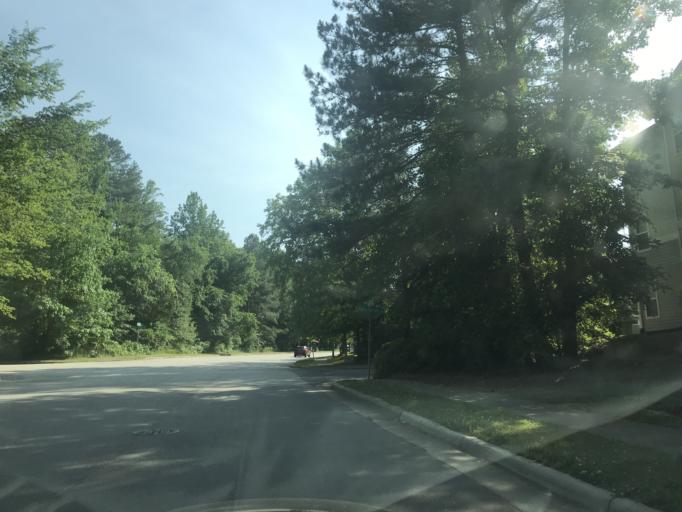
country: US
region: North Carolina
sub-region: Wake County
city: Raleigh
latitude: 35.7773
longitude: -78.5814
